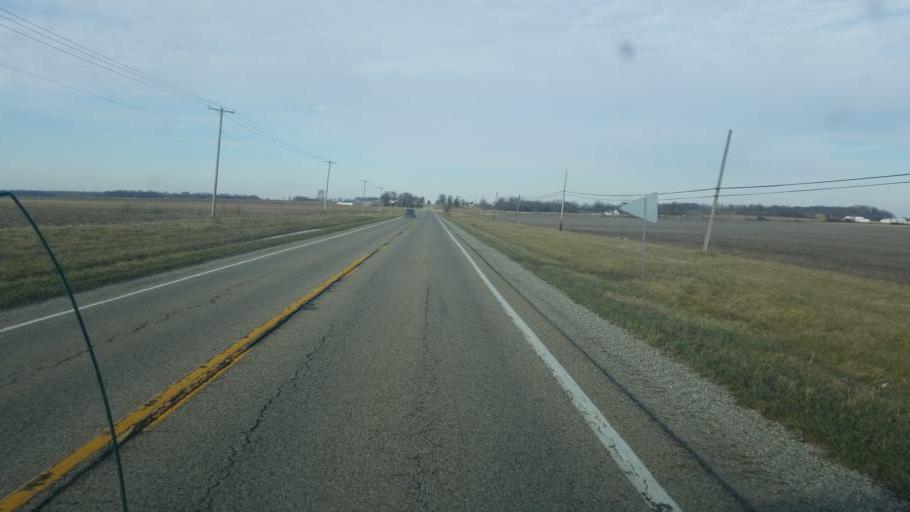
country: US
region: Illinois
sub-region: Lawrence County
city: Bridgeport
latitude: 38.6003
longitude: -87.6943
